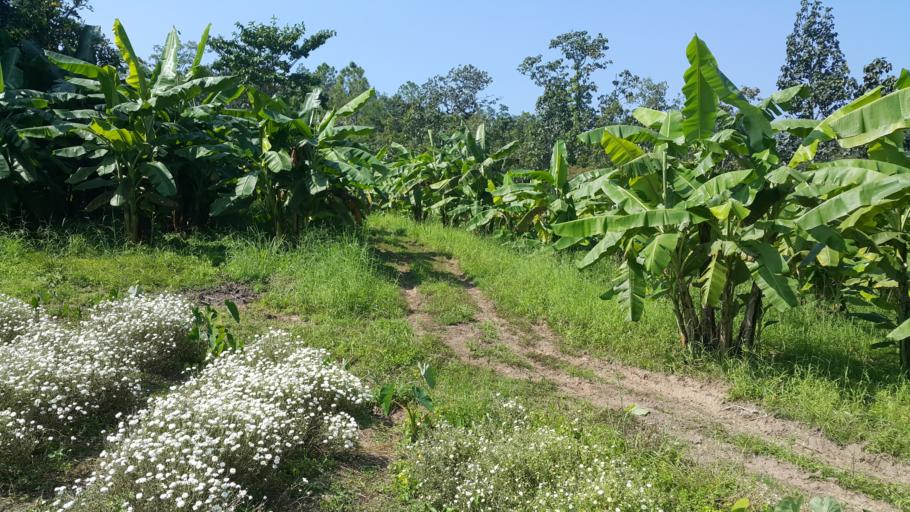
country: TH
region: Chiang Mai
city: Samoeng
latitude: 18.9311
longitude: 98.6152
